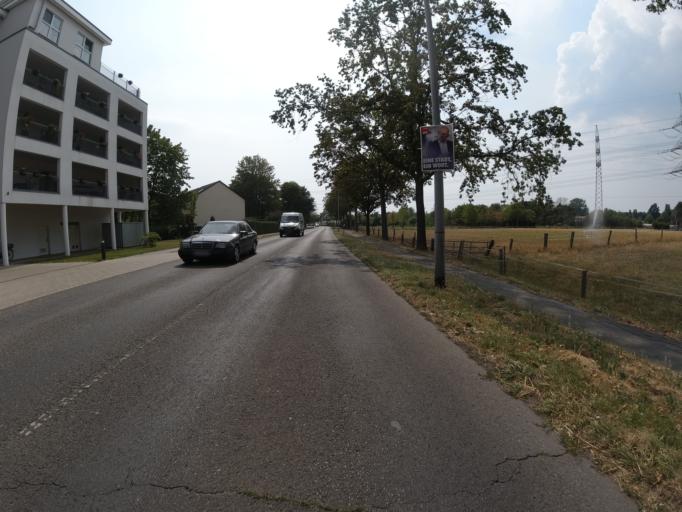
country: DE
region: North Rhine-Westphalia
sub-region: Regierungsbezirk Dusseldorf
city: Moers
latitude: 51.3969
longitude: 6.6449
